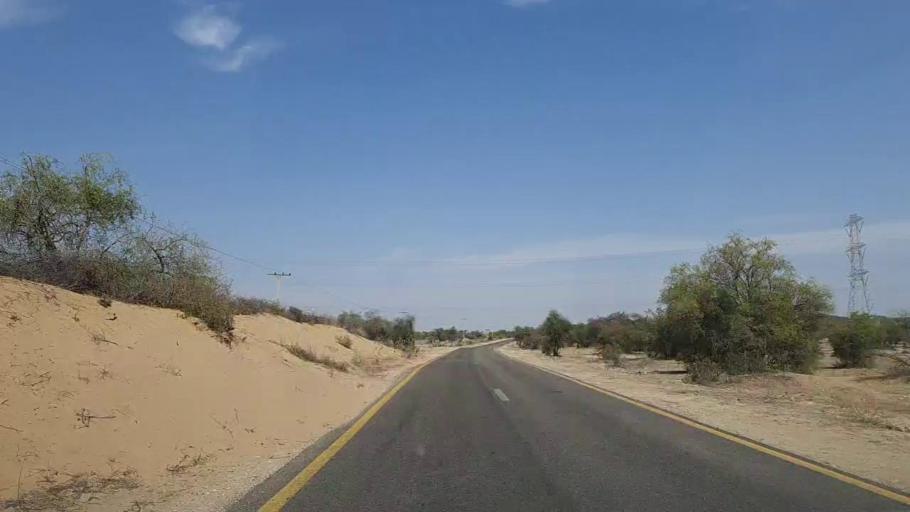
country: PK
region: Sindh
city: Mithi
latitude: 24.8496
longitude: 69.8375
